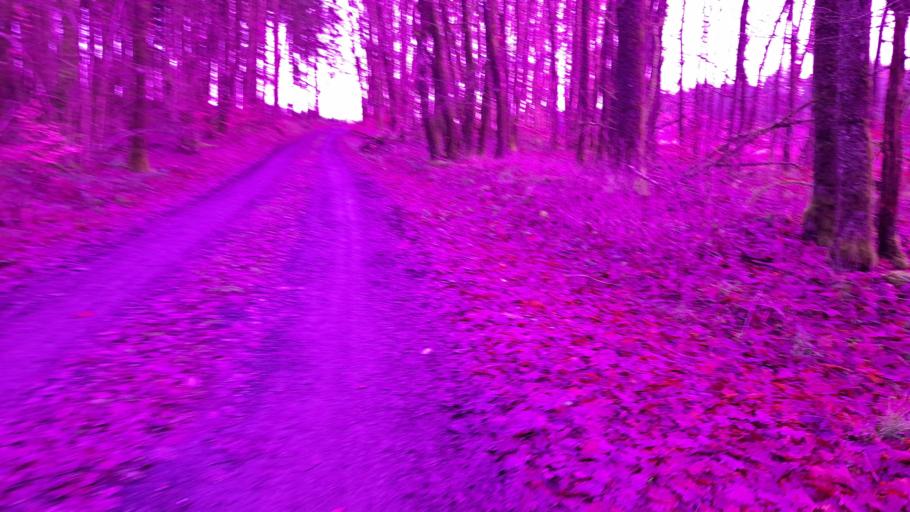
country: DE
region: Rheinland-Pfalz
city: Dasburg
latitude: 50.0847
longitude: 6.1051
